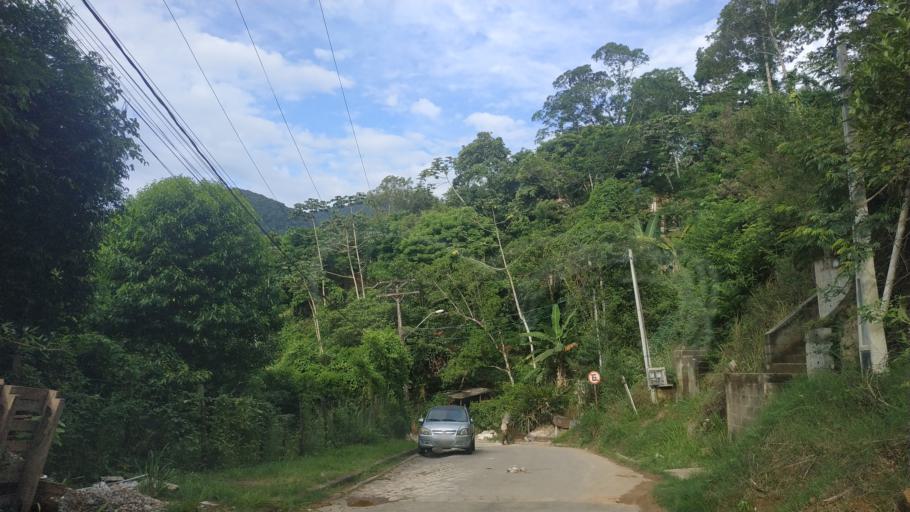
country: BR
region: Sao Paulo
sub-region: Ilhabela
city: Ilhabela
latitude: -23.8293
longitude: -45.3513
